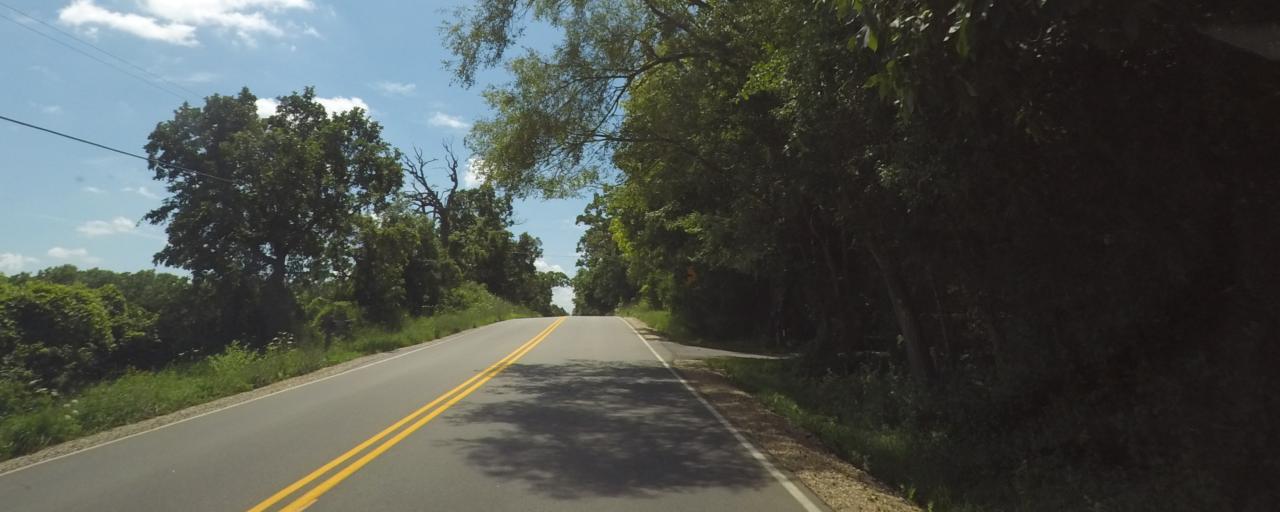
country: US
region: Wisconsin
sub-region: Waukesha County
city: Dousman
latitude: 42.9611
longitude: -88.4674
